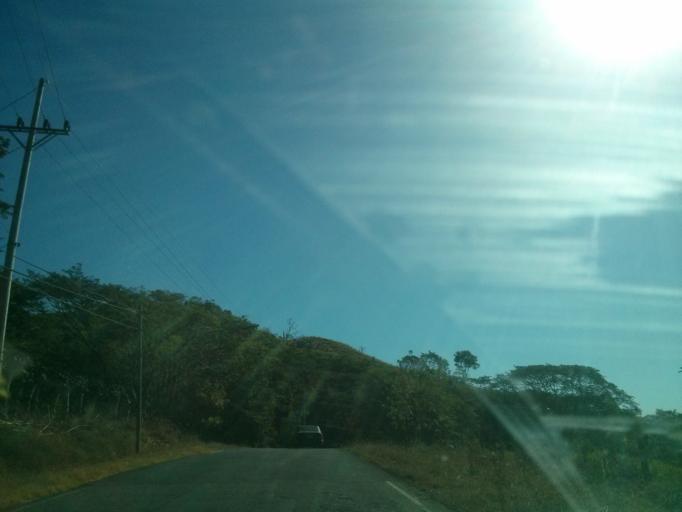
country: CR
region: Puntarenas
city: Paquera
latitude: 9.7681
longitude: -84.9805
